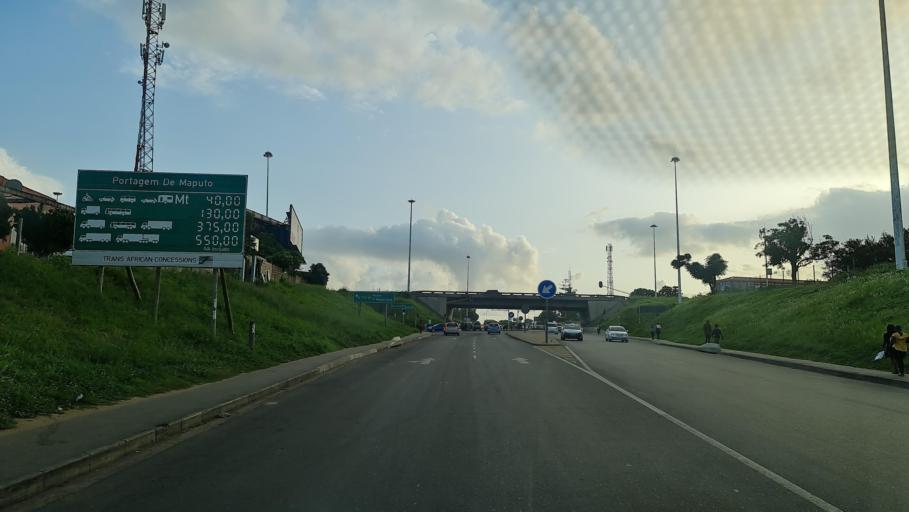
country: MZ
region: Maputo City
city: Maputo
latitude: -25.9447
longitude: 32.5399
